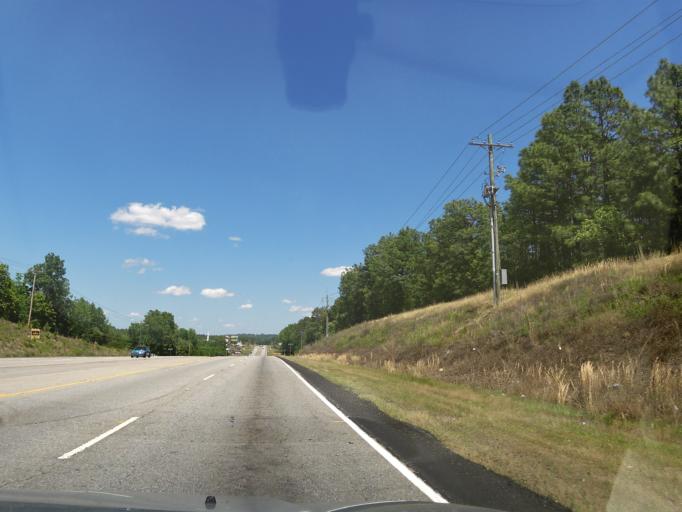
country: US
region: South Carolina
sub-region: Aiken County
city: Gloverville
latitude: 33.5340
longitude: -81.8381
